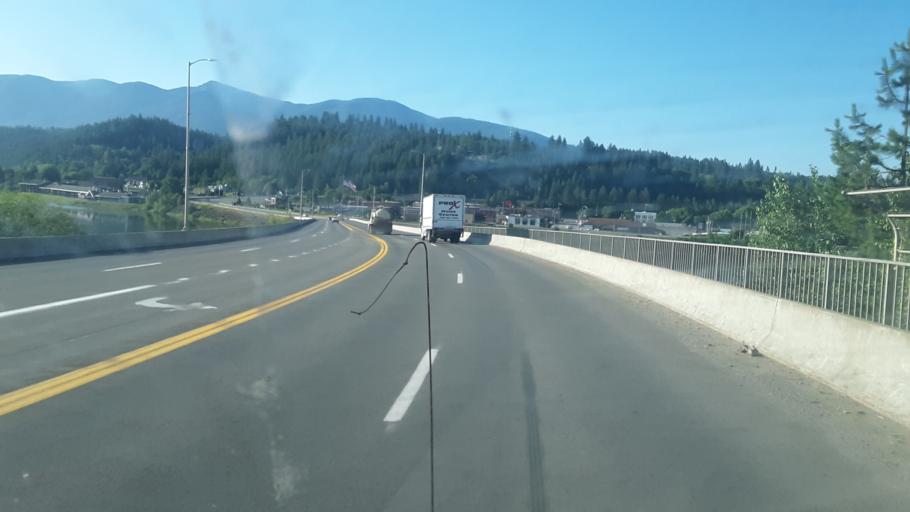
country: US
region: Idaho
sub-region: Boundary County
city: Bonners Ferry
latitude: 48.7015
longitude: -116.3137
